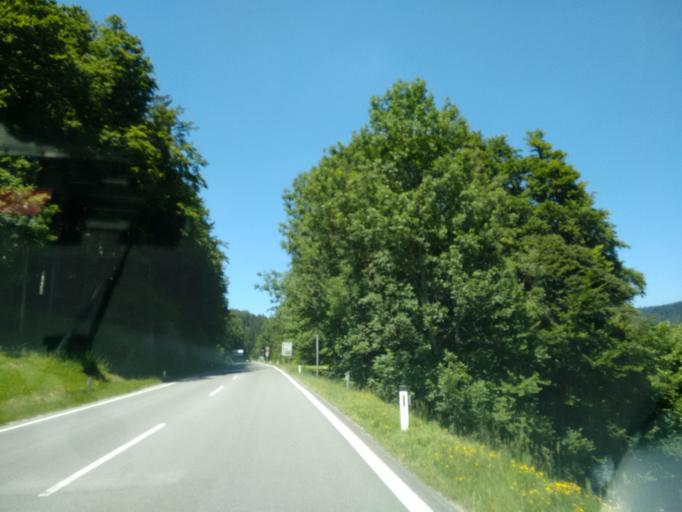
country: AT
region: Styria
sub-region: Politischer Bezirk Liezen
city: Altaussee
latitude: 47.6198
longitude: 13.7579
